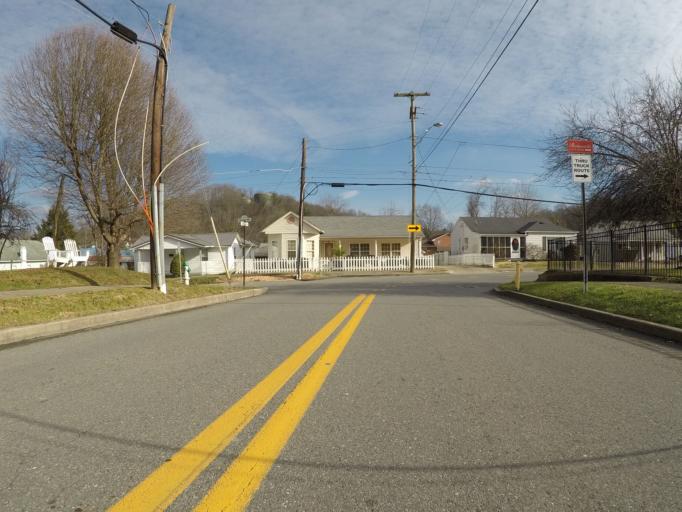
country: US
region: West Virginia
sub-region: Cabell County
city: Barboursville
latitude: 38.4044
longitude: -82.2935
